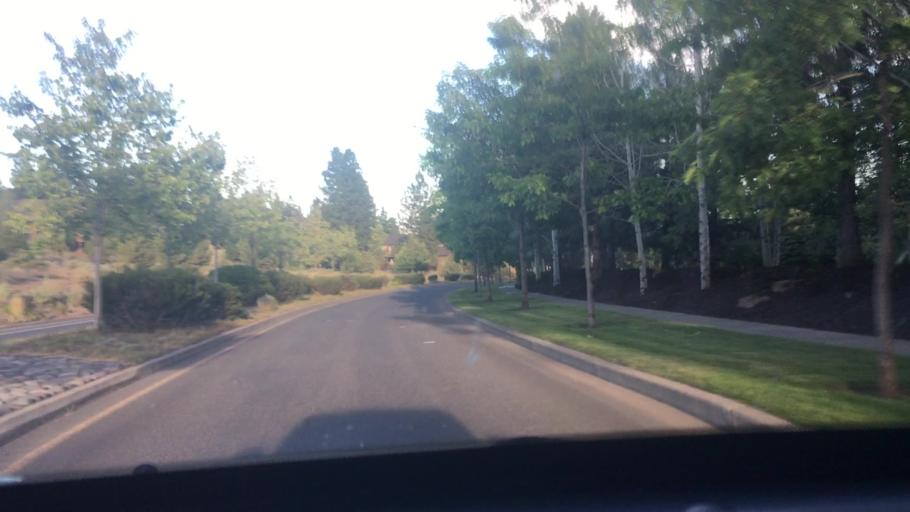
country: US
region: Oregon
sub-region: Deschutes County
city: Bend
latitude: 44.0510
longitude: -121.3469
